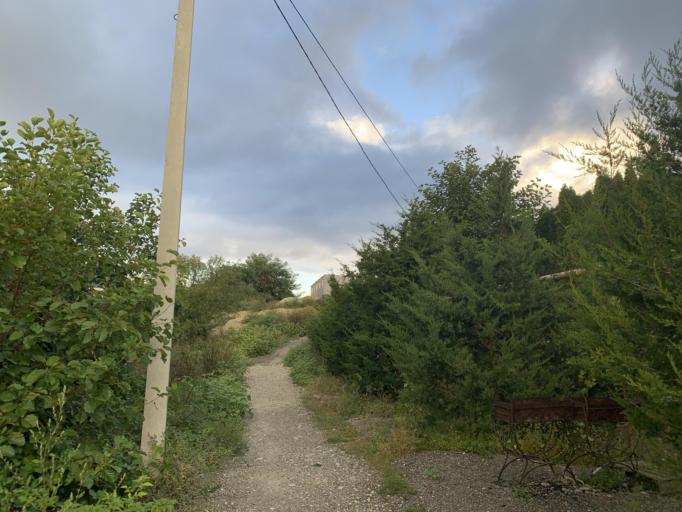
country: RU
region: Krasnodarskiy
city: Nebug
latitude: 44.1673
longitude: 39.0037
